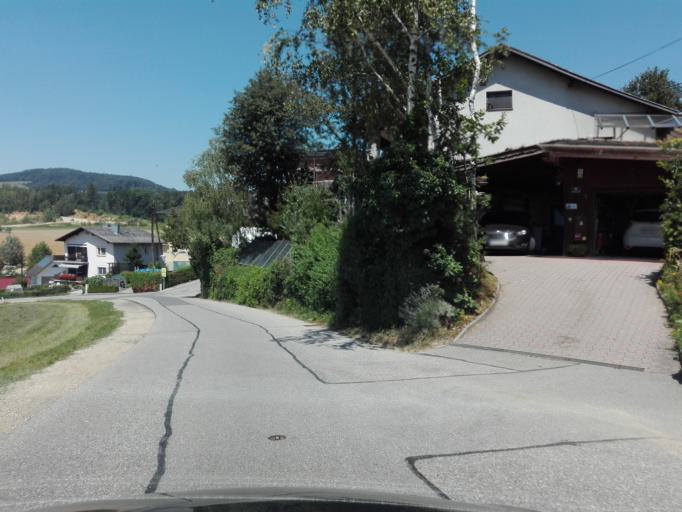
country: AT
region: Upper Austria
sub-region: Politischer Bezirk Urfahr-Umgebung
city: Engerwitzdorf
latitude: 48.2839
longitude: 14.4480
